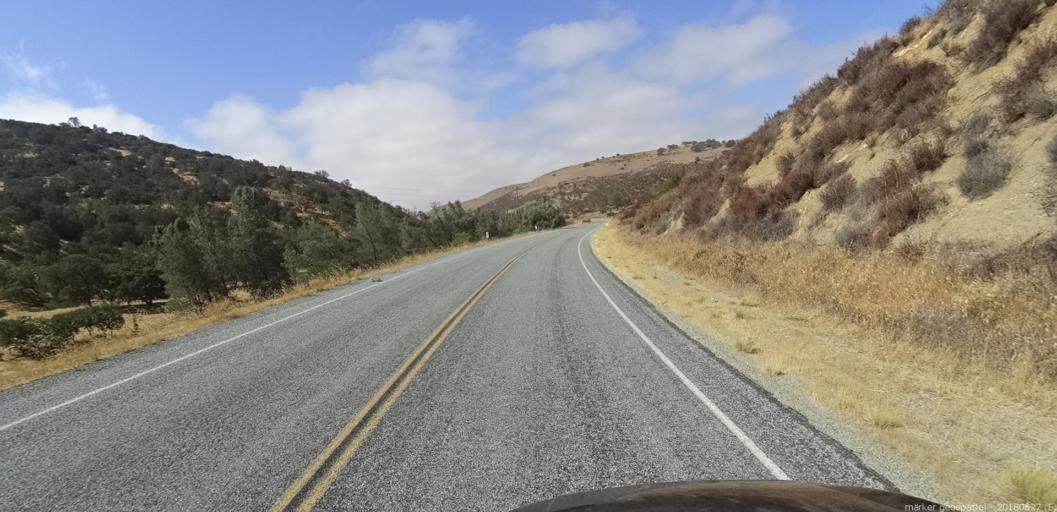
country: US
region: California
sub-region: Monterey County
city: King City
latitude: 36.3015
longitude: -121.0479
